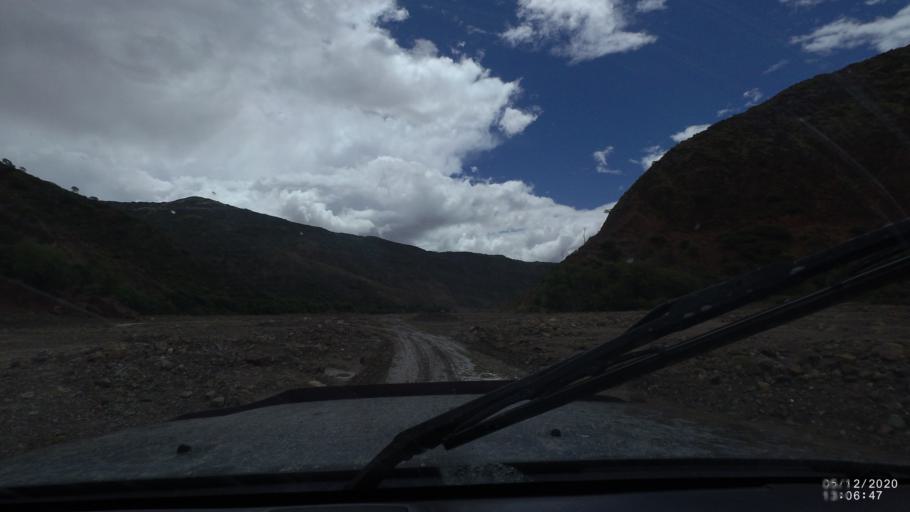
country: BO
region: Cochabamba
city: Sipe Sipe
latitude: -17.5592
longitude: -66.4459
